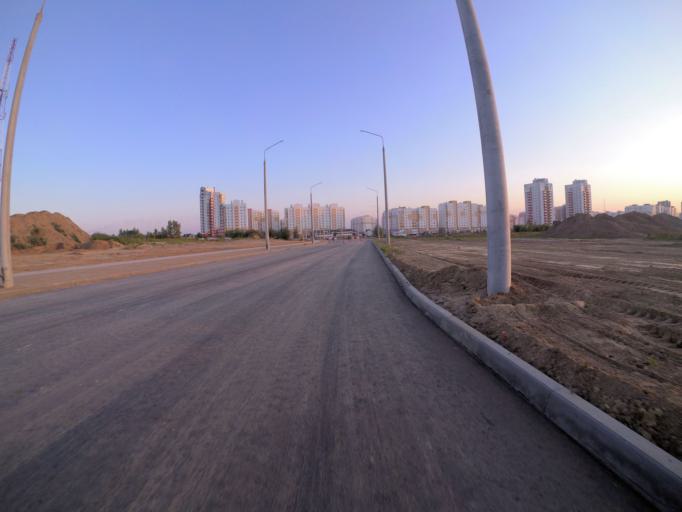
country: BY
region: Grodnenskaya
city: Hrodna
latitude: 53.7156
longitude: 23.8681
